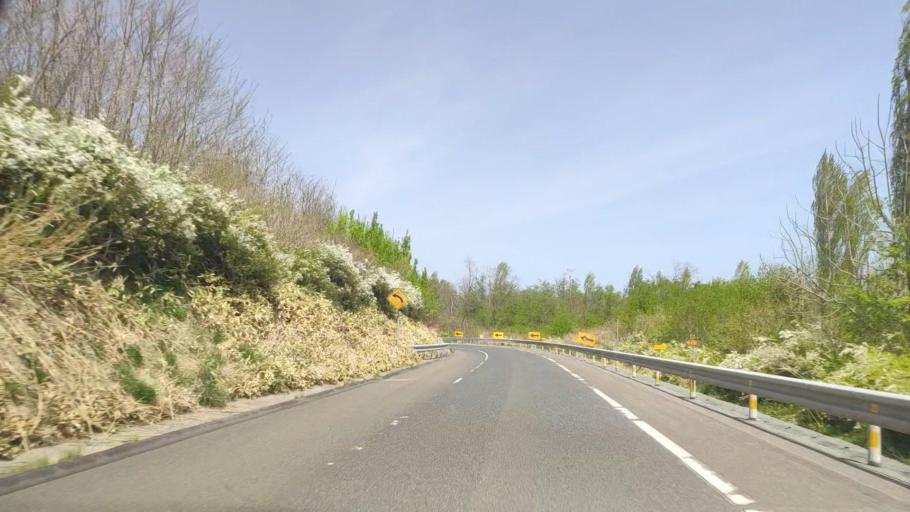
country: JP
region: Aomori
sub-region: Hachinohe Shi
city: Uchimaru
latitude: 40.4934
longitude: 141.4646
